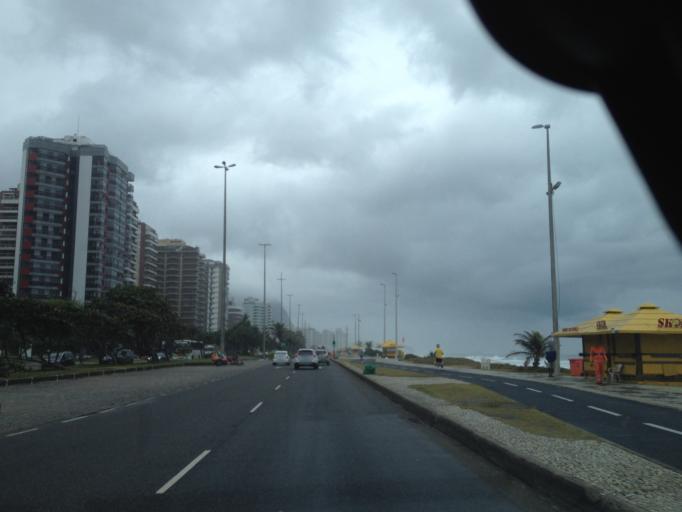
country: BR
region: Rio de Janeiro
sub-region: Rio De Janeiro
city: Rio de Janeiro
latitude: -23.0106
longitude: -43.3586
